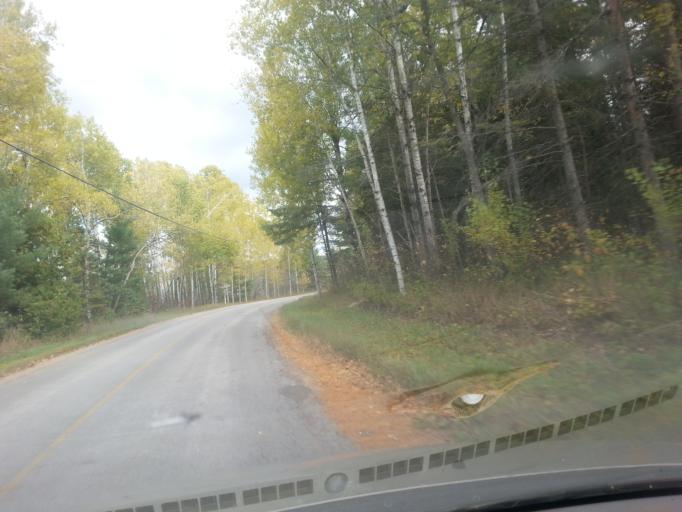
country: CA
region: Ontario
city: Pembroke
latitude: 45.5030
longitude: -77.0120
